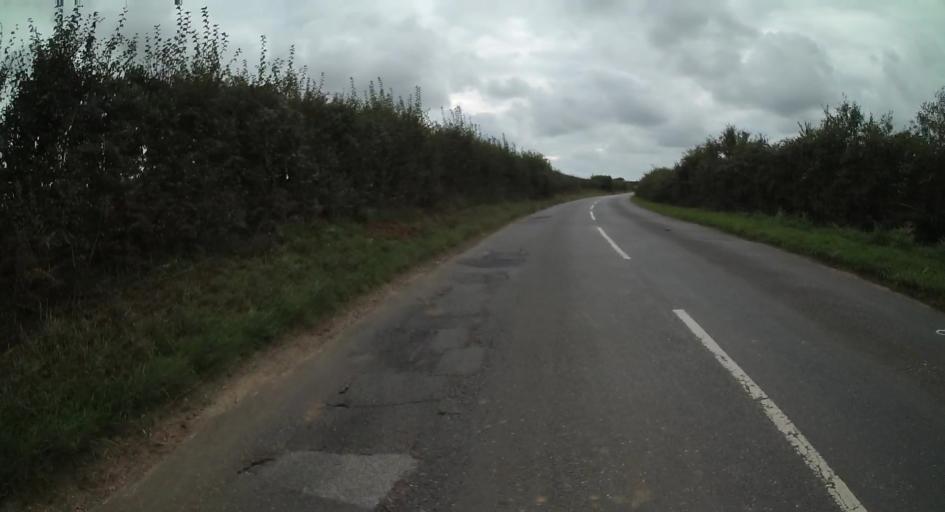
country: GB
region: England
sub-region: Isle of Wight
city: Niton
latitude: 50.6249
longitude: -1.2637
